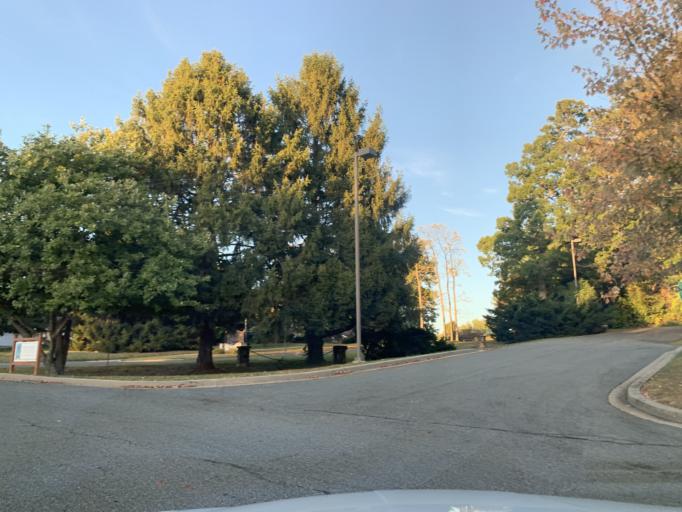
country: US
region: Maryland
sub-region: Harford County
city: South Bel Air
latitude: 39.5317
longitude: -76.3417
